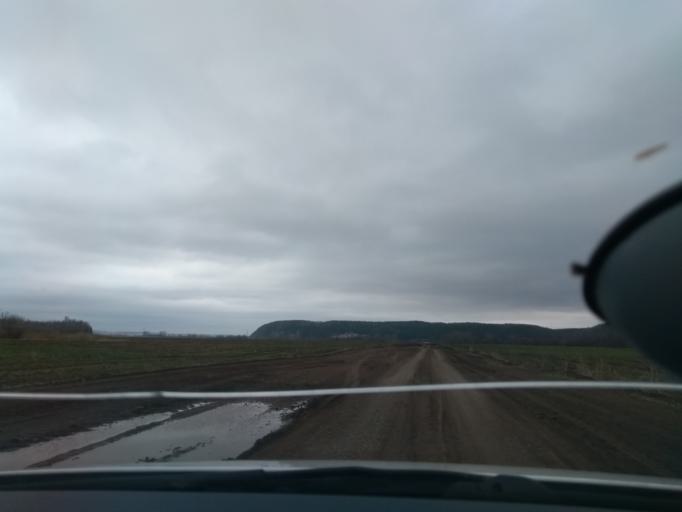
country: RU
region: Perm
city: Orda
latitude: 57.2501
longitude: 56.6195
